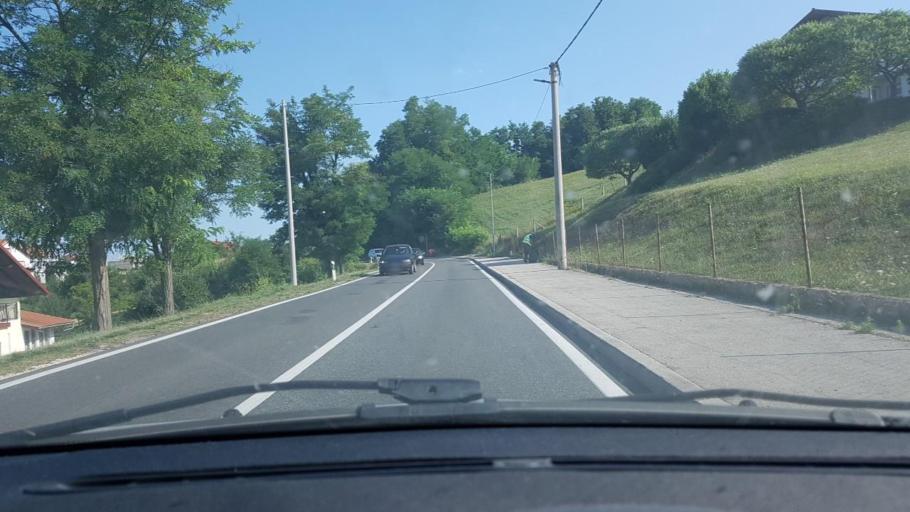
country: BA
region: Federation of Bosnia and Herzegovina
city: Ostrozac
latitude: 44.9116
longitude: 15.9313
